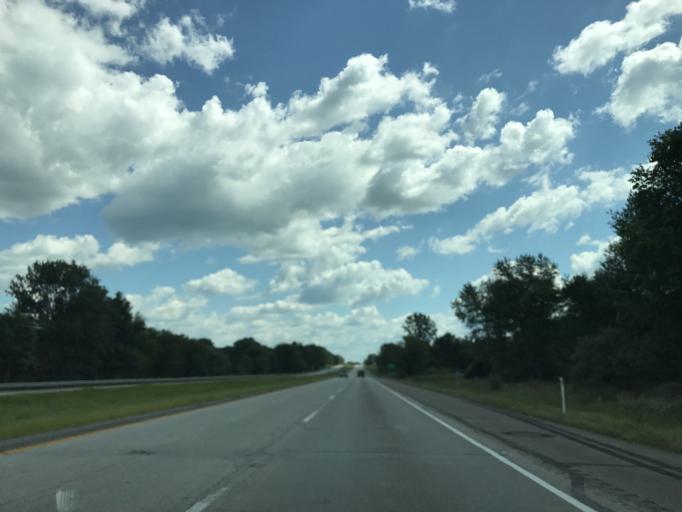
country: US
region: Indiana
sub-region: Starke County
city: Koontz Lake
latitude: 41.3644
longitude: -86.4065
